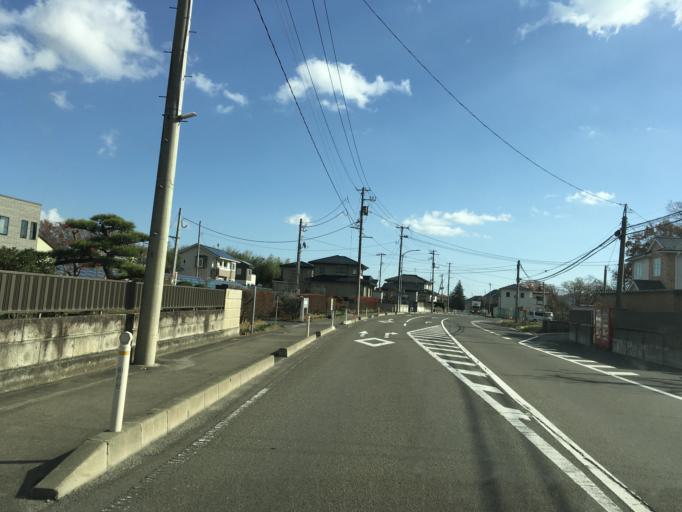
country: JP
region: Miyagi
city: Sendai
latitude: 38.2873
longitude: 140.7505
